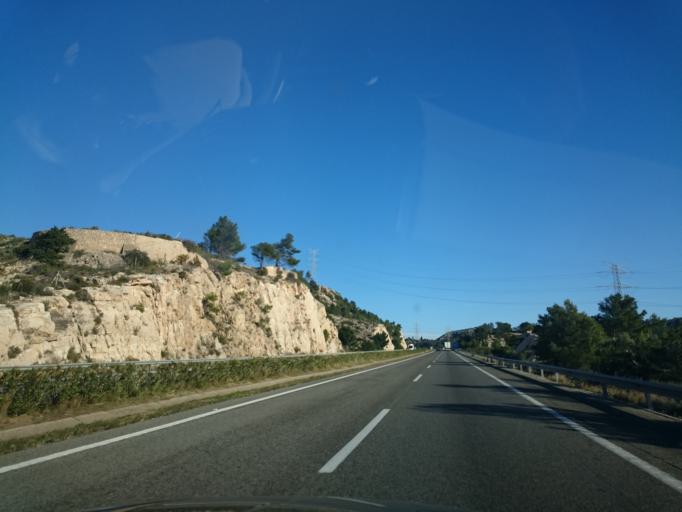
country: ES
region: Catalonia
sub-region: Provincia de Tarragona
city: l'Ametlla de Mar
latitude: 40.9614
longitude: 0.8693
